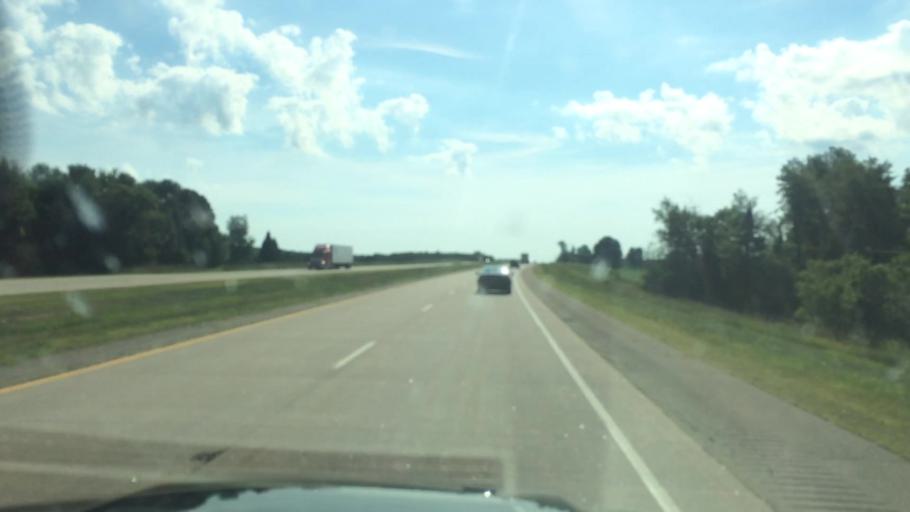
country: US
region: Wisconsin
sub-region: Shawano County
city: Wittenberg
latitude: 44.8038
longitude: -89.0083
